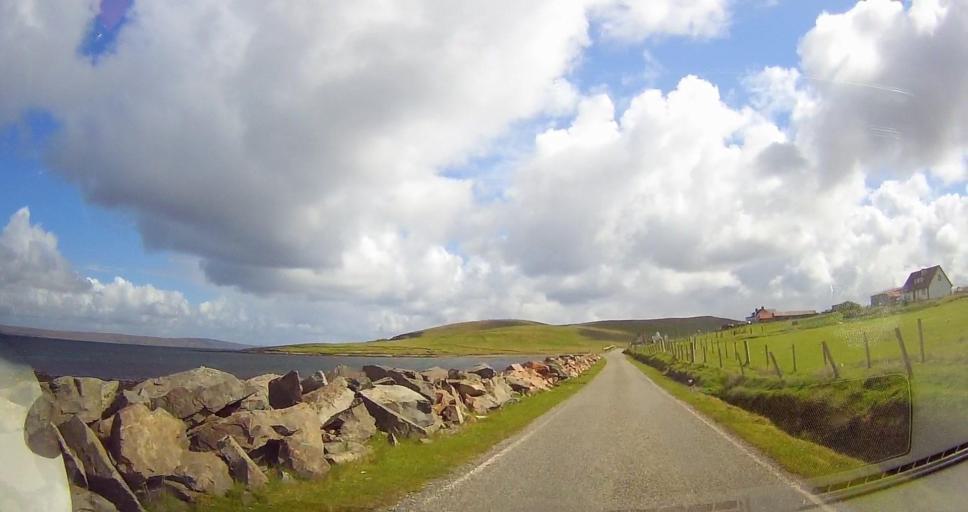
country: GB
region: Scotland
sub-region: Shetland Islands
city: Lerwick
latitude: 60.5808
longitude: -1.3344
